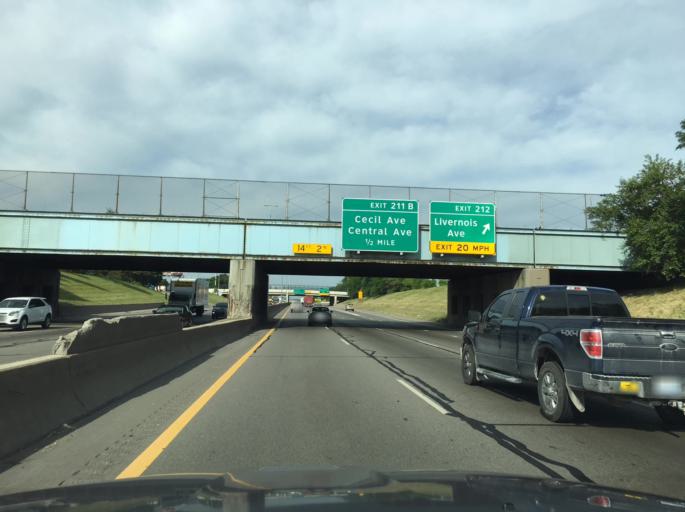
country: US
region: Michigan
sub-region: Wayne County
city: Dearborn
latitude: 42.3388
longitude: -83.1217
